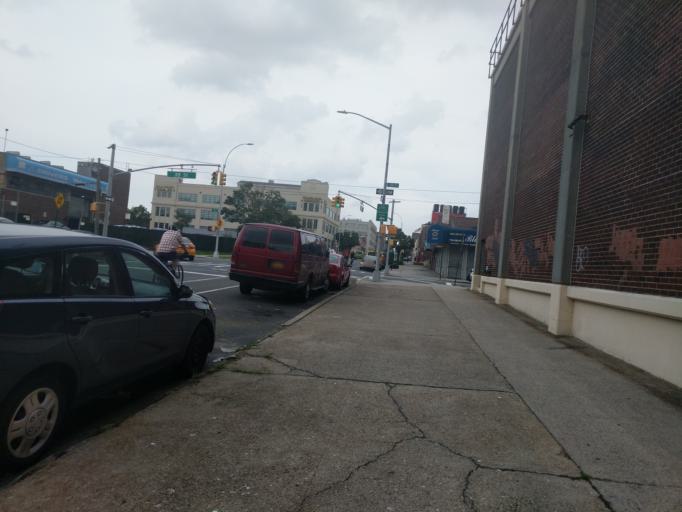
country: US
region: New York
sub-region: Queens County
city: Long Island City
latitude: 40.7462
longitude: -73.9299
